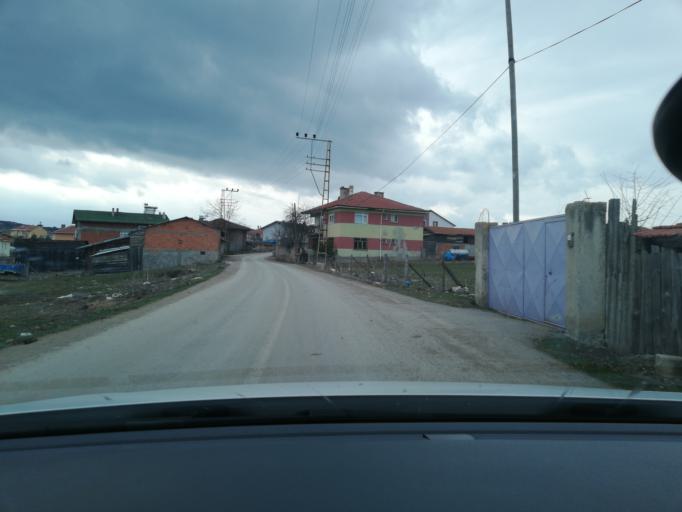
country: TR
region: Bolu
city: Gerede
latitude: 40.6908
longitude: 32.2139
